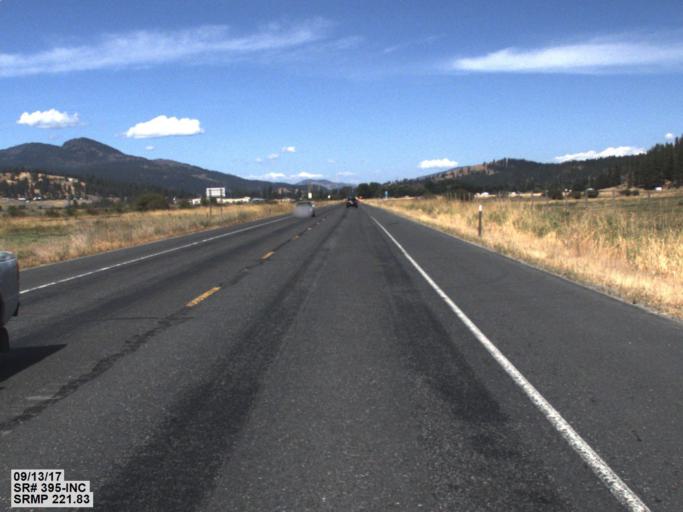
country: US
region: Washington
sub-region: Stevens County
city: Colville
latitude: 48.4402
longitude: -117.8664
